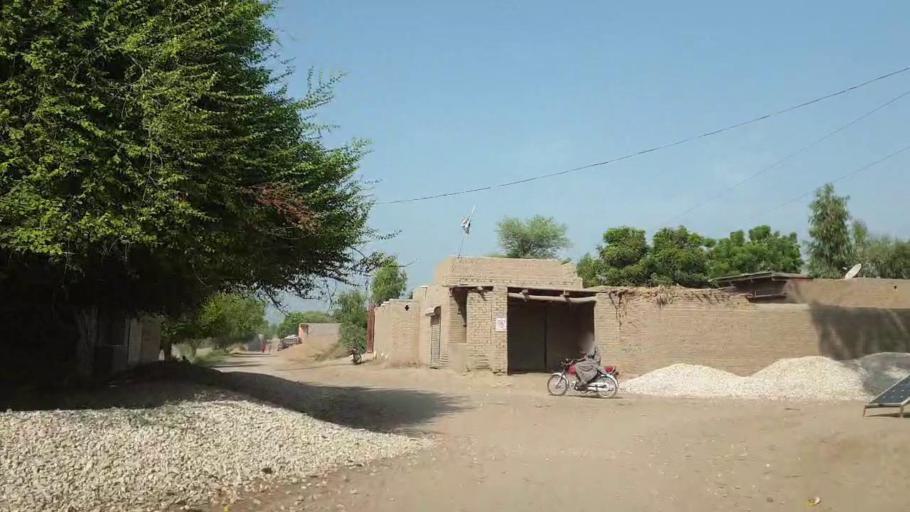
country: PK
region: Sindh
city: Larkana
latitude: 27.4805
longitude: 68.2520
